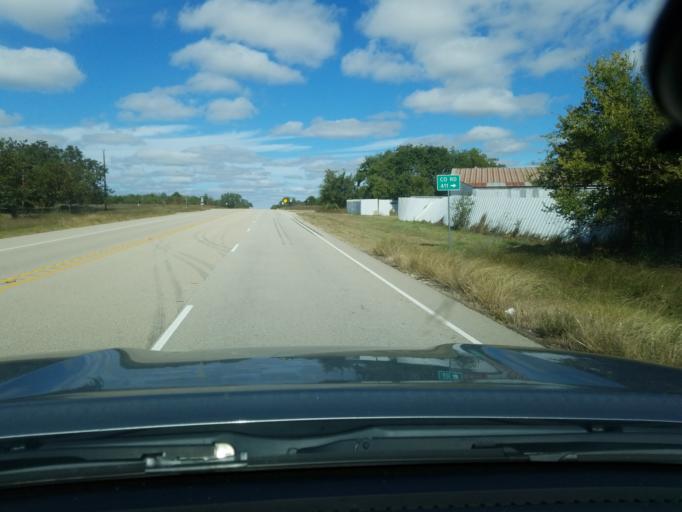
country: US
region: Texas
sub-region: Hamilton County
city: Hamilton
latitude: 31.5916
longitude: -98.1568
